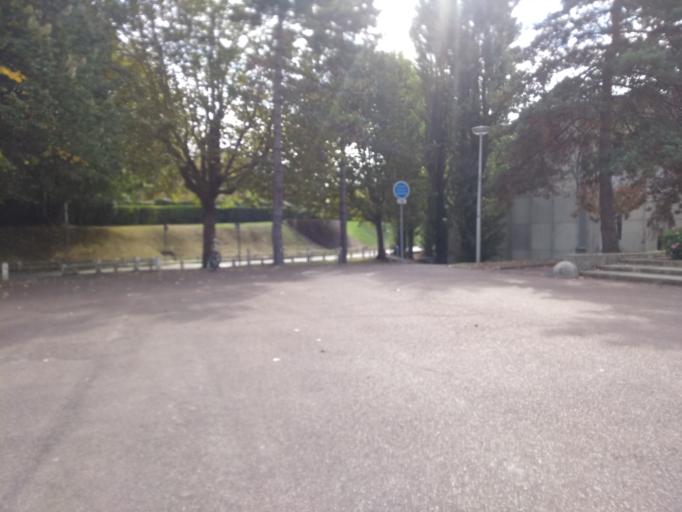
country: FR
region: Aquitaine
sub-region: Departement de la Gironde
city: Talence
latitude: 44.8249
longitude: -0.6048
